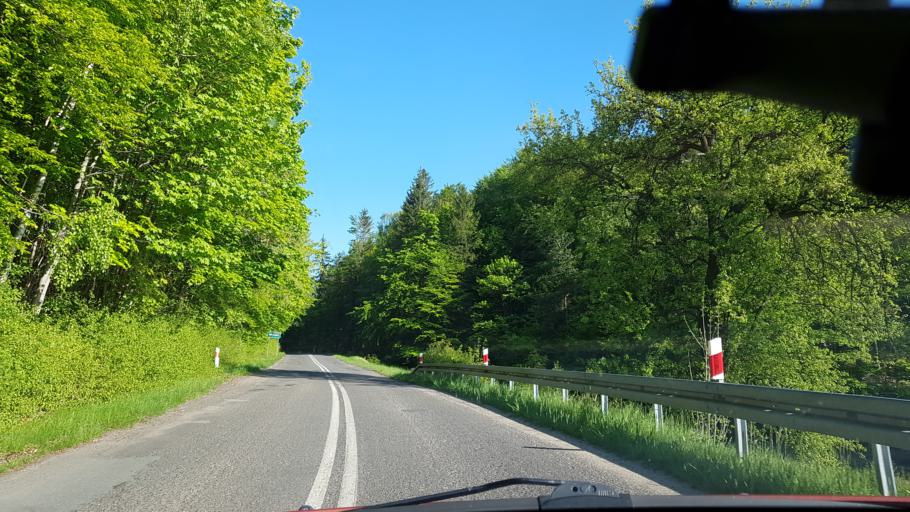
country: PL
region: Lower Silesian Voivodeship
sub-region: Powiat klodzki
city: Bozkow
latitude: 50.5786
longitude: 16.5951
